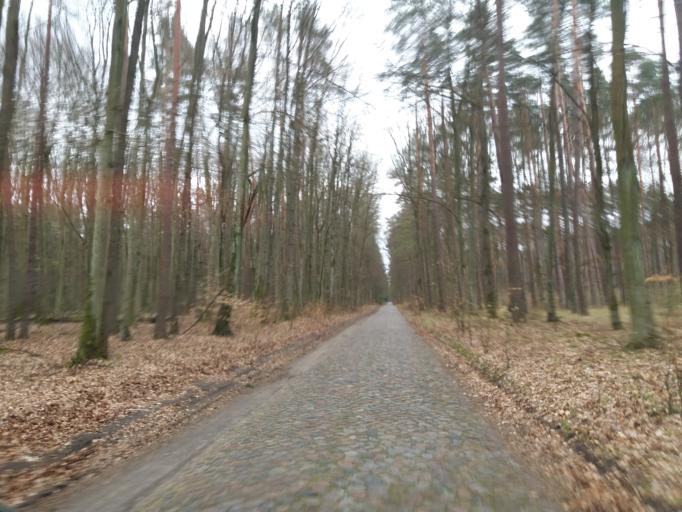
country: PL
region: West Pomeranian Voivodeship
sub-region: Powiat choszczenski
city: Drawno
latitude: 53.1032
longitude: 15.8487
